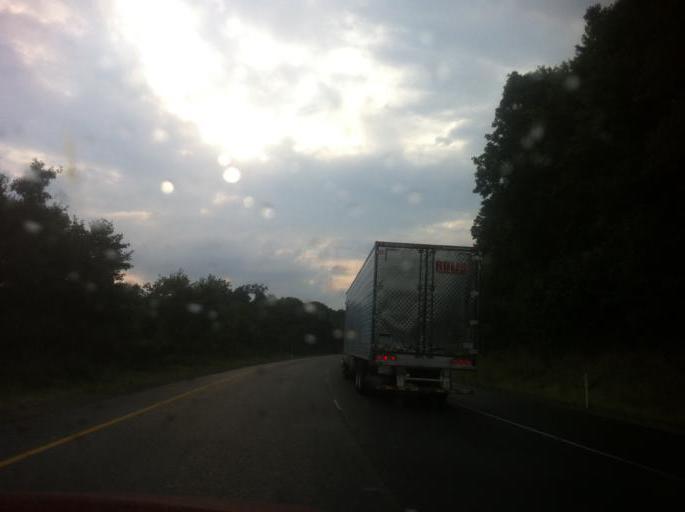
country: US
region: Pennsylvania
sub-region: Clarion County
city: Knox
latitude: 41.1965
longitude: -79.4783
